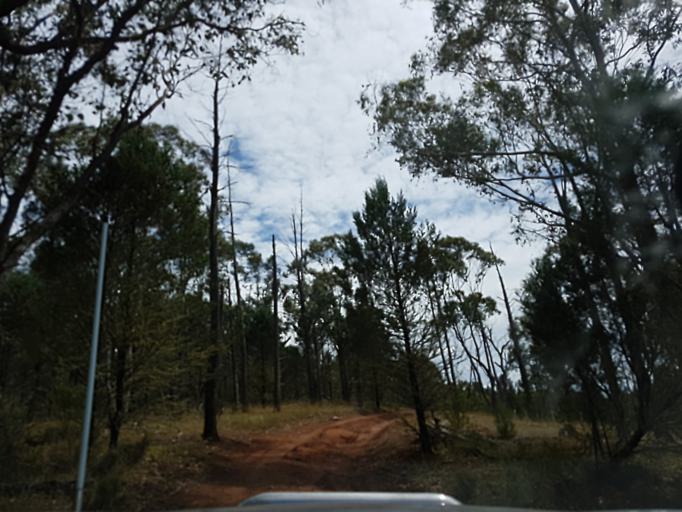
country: AU
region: New South Wales
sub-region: Snowy River
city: Jindabyne
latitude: -36.9406
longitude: 148.3962
